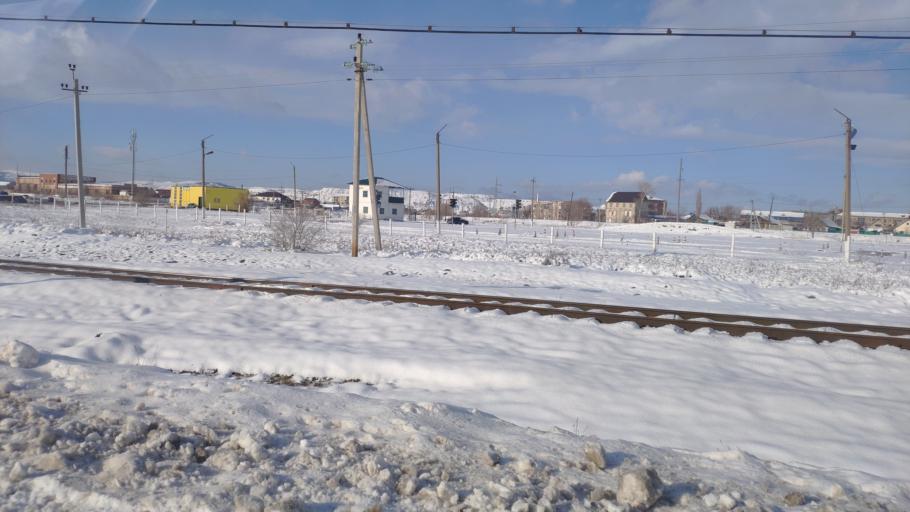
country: RU
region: Bashkortostan
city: Sibay
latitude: 52.7048
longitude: 58.6645
